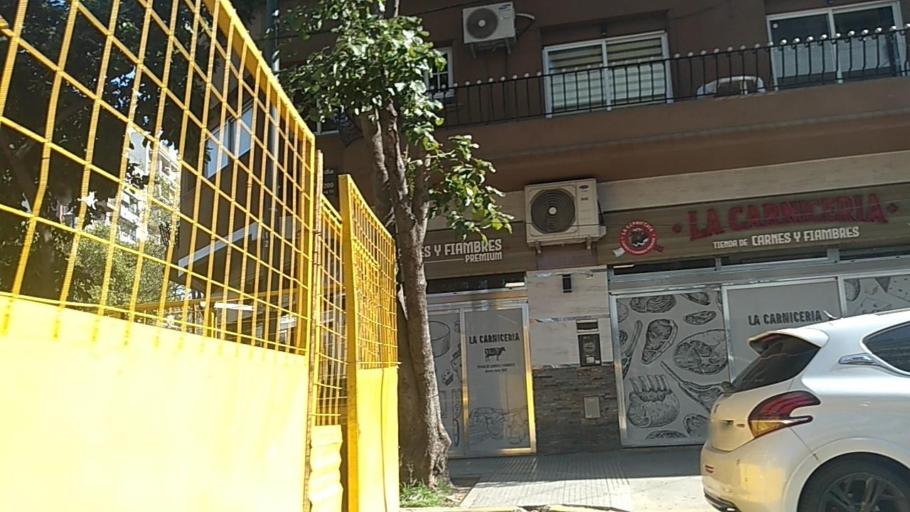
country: AR
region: Buenos Aires F.D.
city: Villa Santa Rita
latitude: -34.6128
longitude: -58.4923
